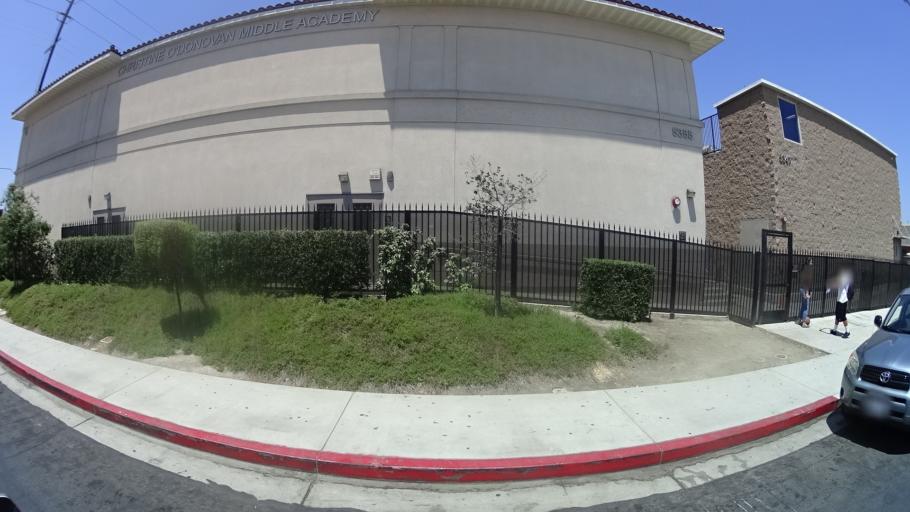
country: US
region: California
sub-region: Los Angeles County
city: View Park-Windsor Hills
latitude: 33.9936
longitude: -118.3215
